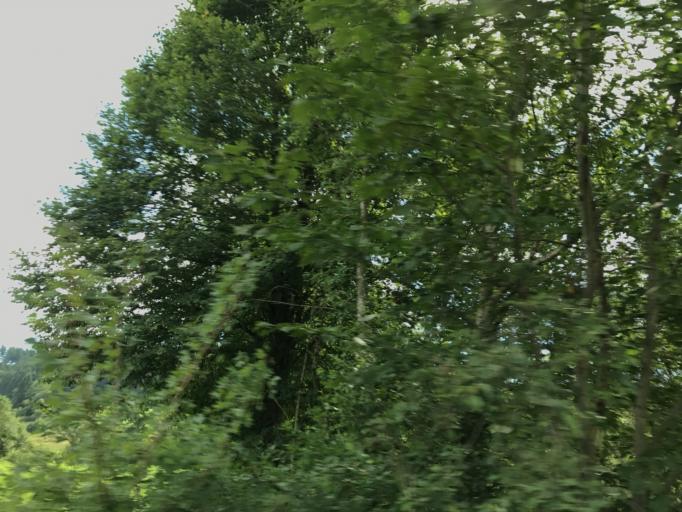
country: DE
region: Bavaria
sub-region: Swabia
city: Heimenkirch
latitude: 47.6549
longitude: 9.9348
